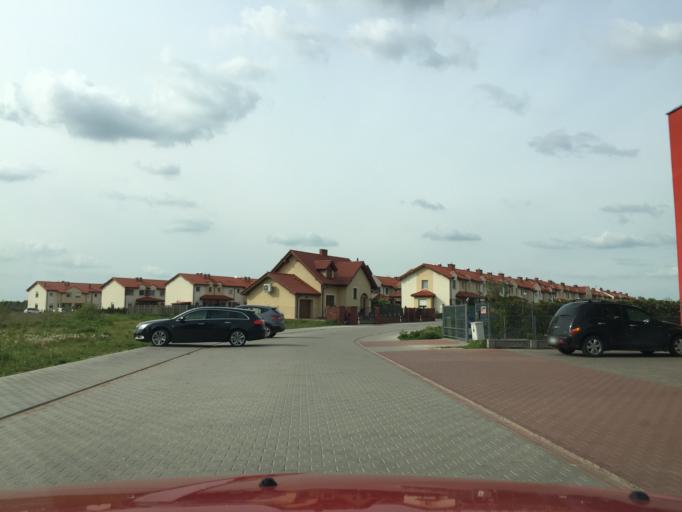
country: PL
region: Greater Poland Voivodeship
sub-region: Powiat poznanski
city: Plewiska
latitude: 52.3895
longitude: 16.7722
